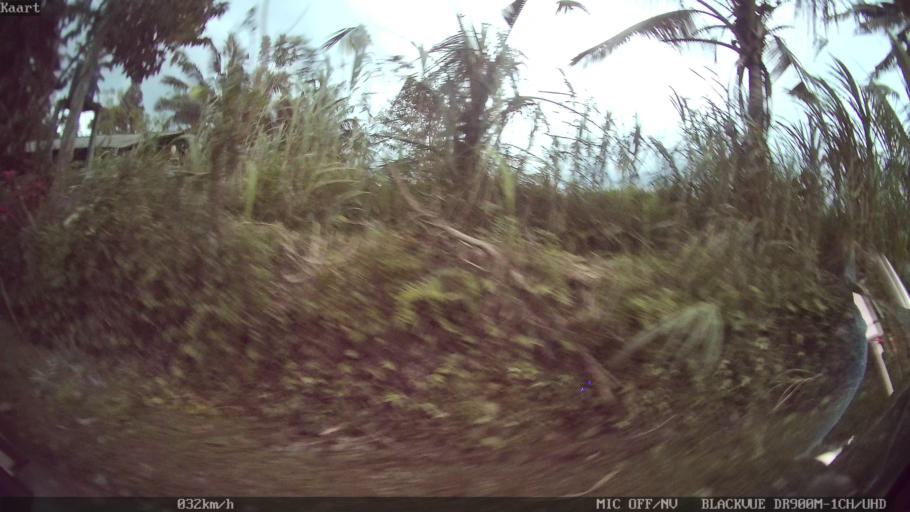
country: ID
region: Bali
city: Banjar Wangsian
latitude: -8.4577
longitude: 115.4089
